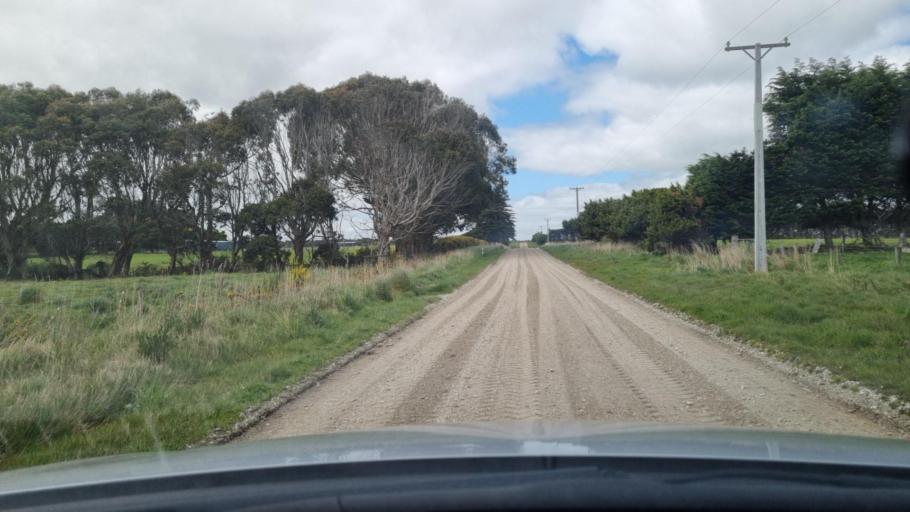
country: NZ
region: Southland
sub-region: Invercargill City
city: Invercargill
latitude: -46.4343
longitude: 168.4068
